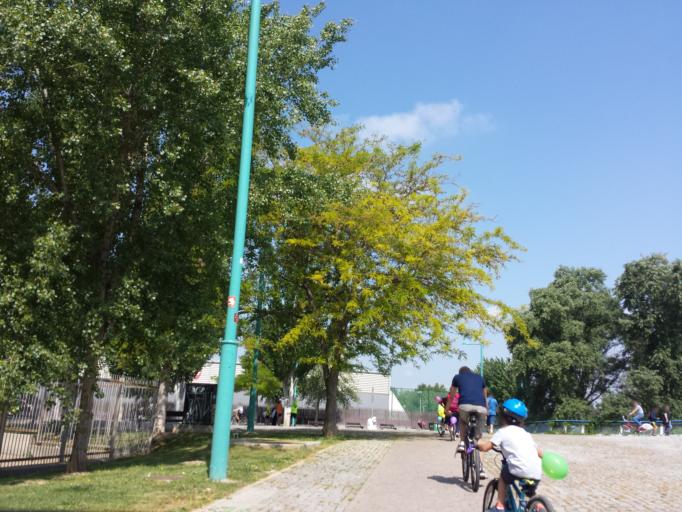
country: ES
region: Aragon
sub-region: Provincia de Zaragoza
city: Almozara
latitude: 41.6636
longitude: -0.8956
